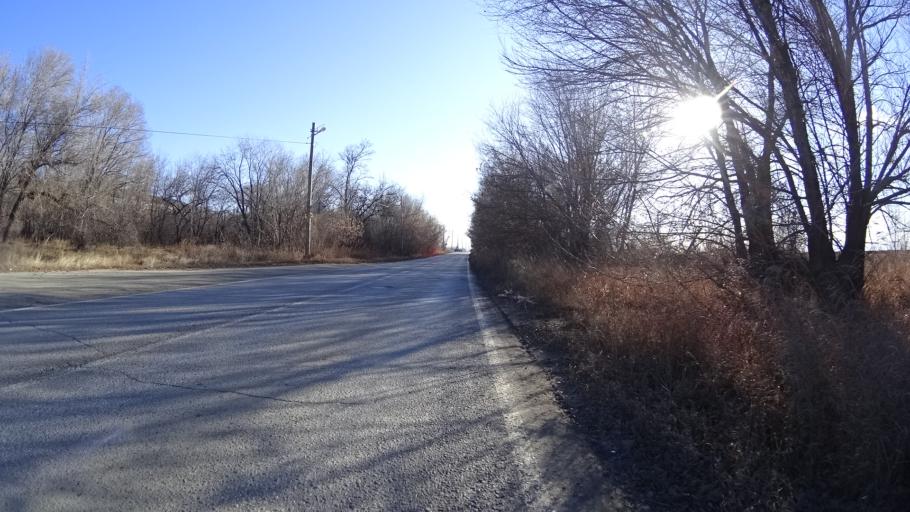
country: RU
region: Chelyabinsk
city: Troitsk
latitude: 54.0476
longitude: 61.6207
